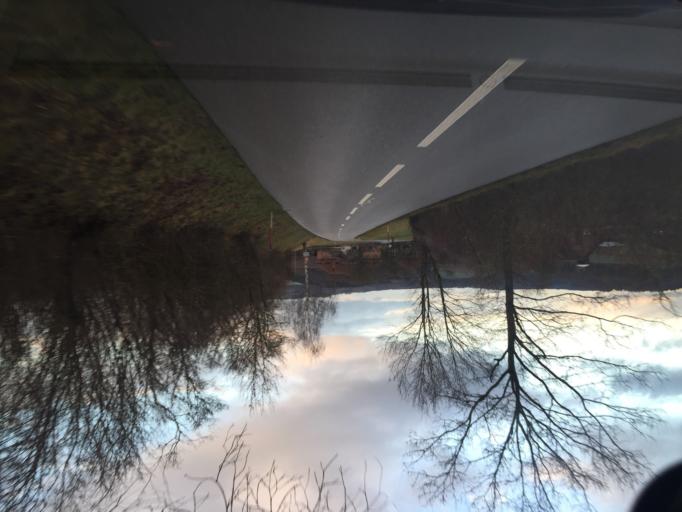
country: DE
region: Baden-Wuerttemberg
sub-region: Freiburg Region
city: Busingen
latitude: 47.7121
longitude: 8.6844
